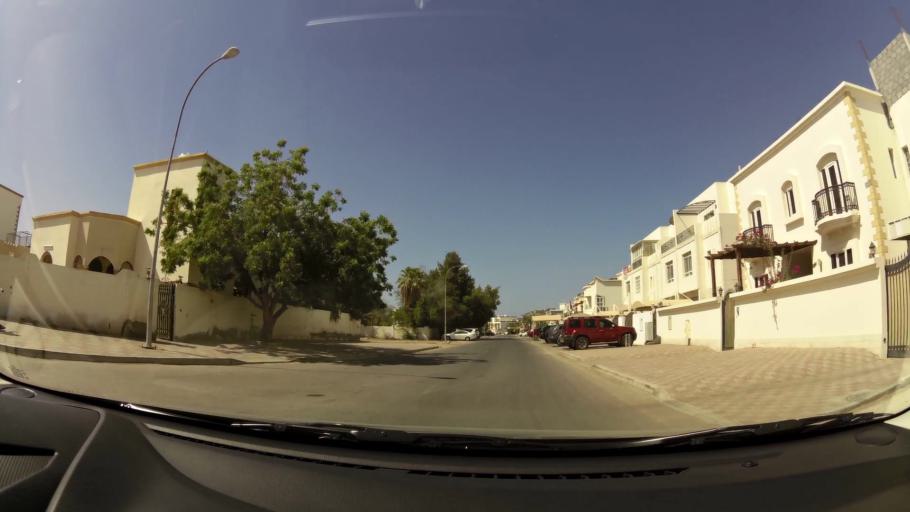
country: OM
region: Muhafazat Masqat
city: Bawshar
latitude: 23.5998
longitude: 58.3820
